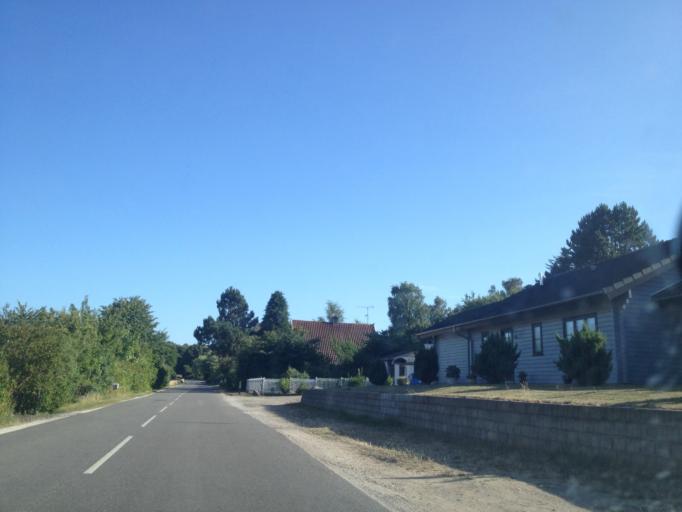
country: DK
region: Capital Region
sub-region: Gribskov Kommune
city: Helsinge
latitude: 56.0505
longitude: 12.1095
